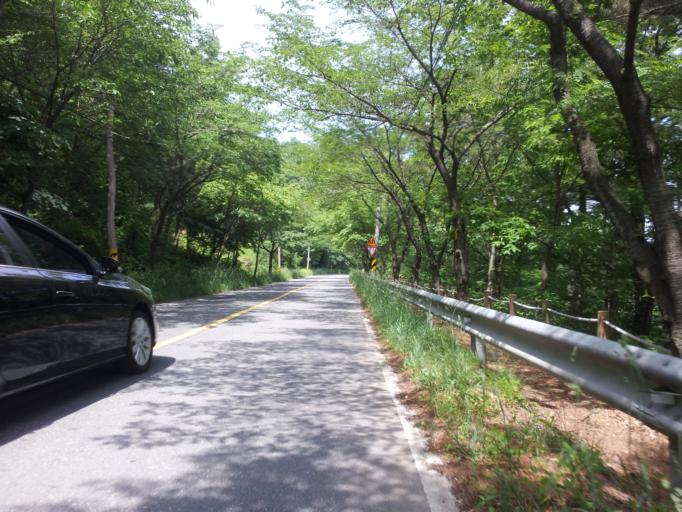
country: KR
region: Daejeon
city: Sintansin
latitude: 36.4351
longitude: 127.4699
